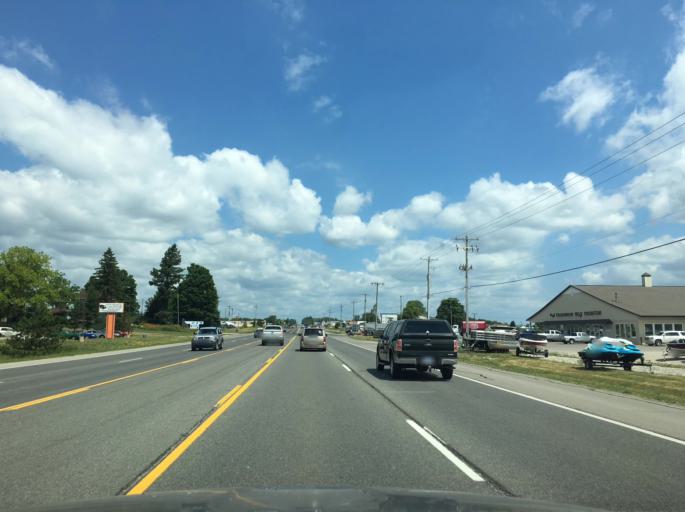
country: US
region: Michigan
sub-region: Grand Traverse County
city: Traverse City
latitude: 44.6884
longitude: -85.6563
